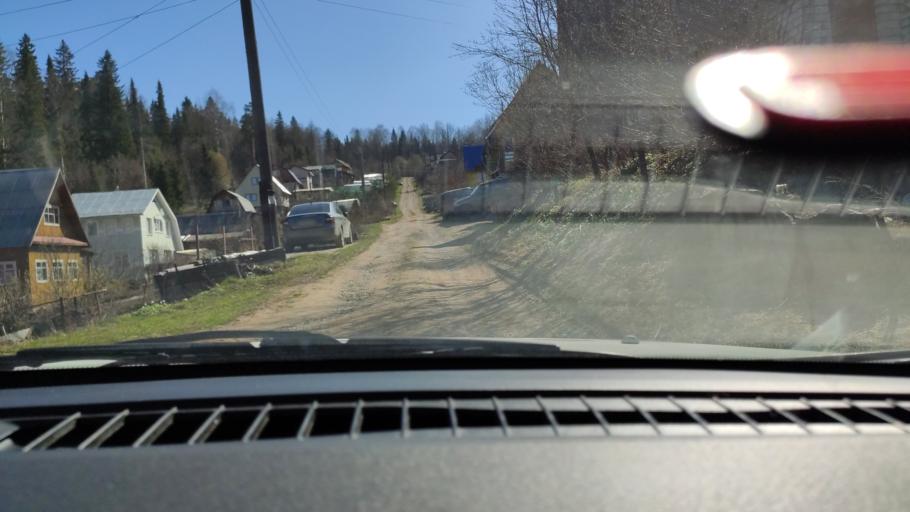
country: RU
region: Perm
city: Bershet'
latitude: 57.7226
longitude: 56.4091
